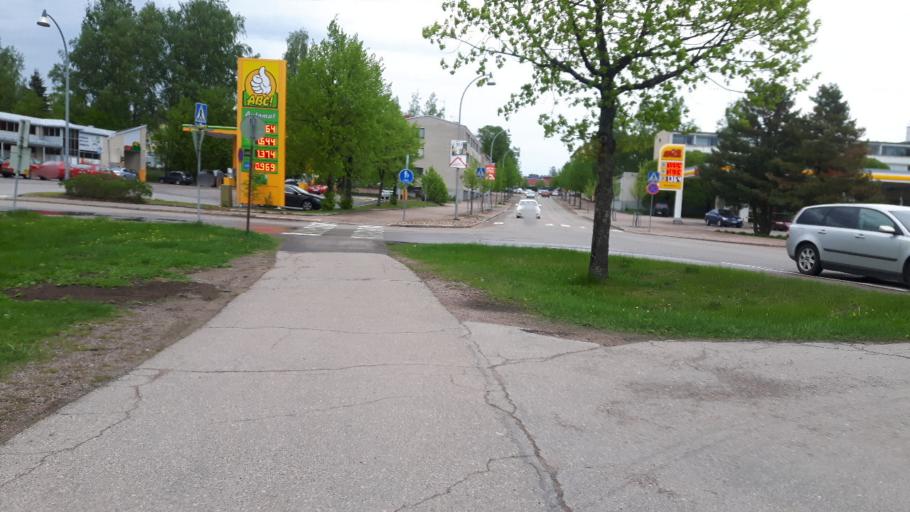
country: FI
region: Kymenlaakso
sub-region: Kotka-Hamina
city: Hamina
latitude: 60.5655
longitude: 27.1900
